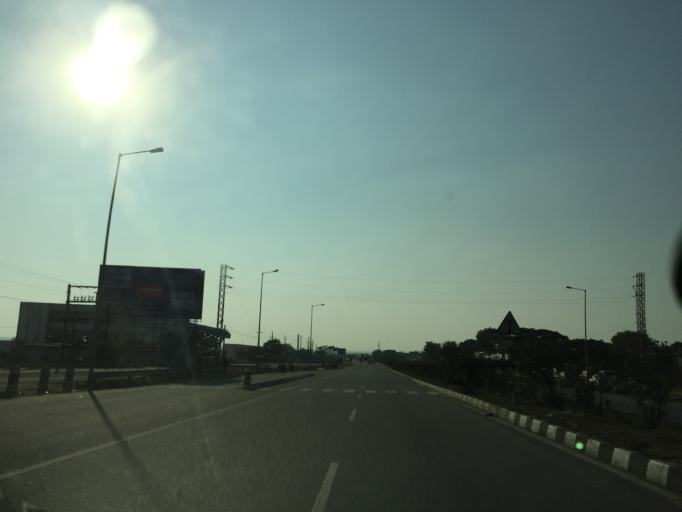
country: IN
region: Telangana
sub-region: Nalgonda
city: Bhongir
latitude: 17.5038
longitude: 78.8589
